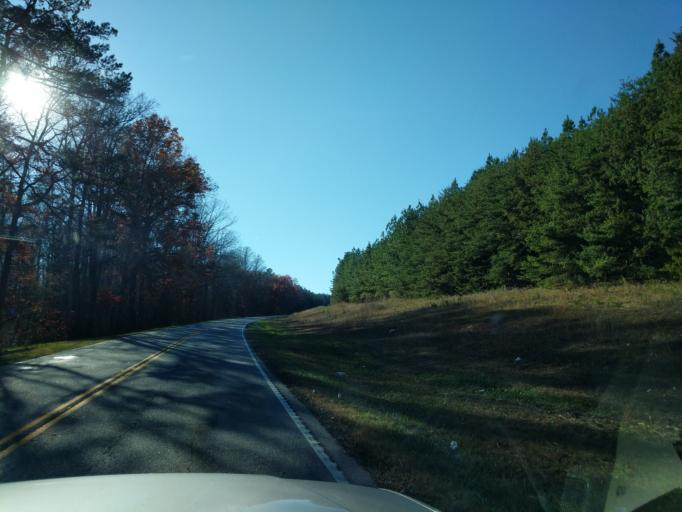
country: US
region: South Carolina
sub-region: Spartanburg County
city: Landrum
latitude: 35.1287
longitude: -82.1222
